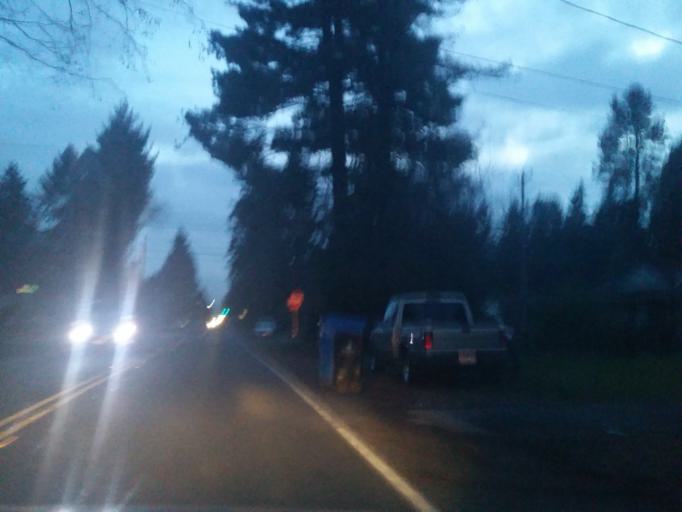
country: US
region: Washington
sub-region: King County
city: Shoreline
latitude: 47.7600
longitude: -122.3189
